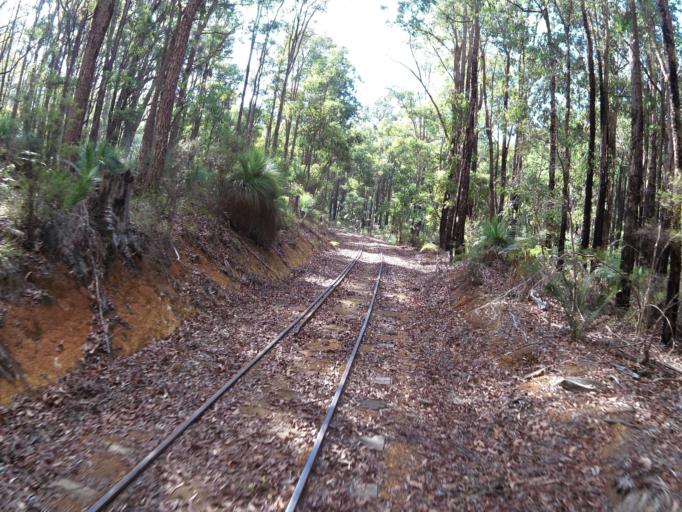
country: AU
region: Western Australia
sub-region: Waroona
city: Waroona
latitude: -32.7316
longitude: 116.1140
